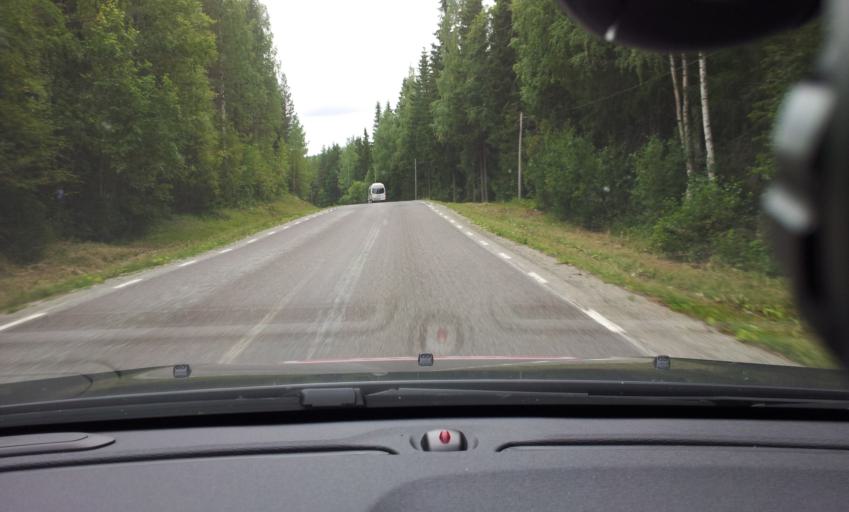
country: SE
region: Jaemtland
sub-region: Braecke Kommun
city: Braecke
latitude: 63.0066
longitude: 15.1981
